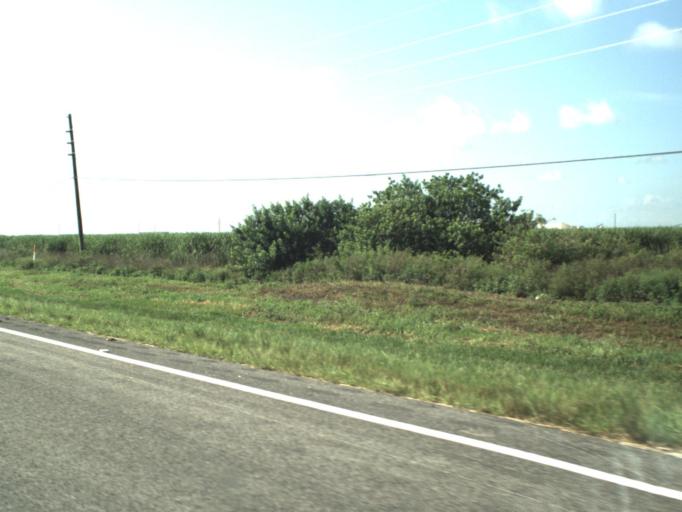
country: US
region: Florida
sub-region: Palm Beach County
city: Belle Glade Camp
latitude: 26.5093
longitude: -80.6731
